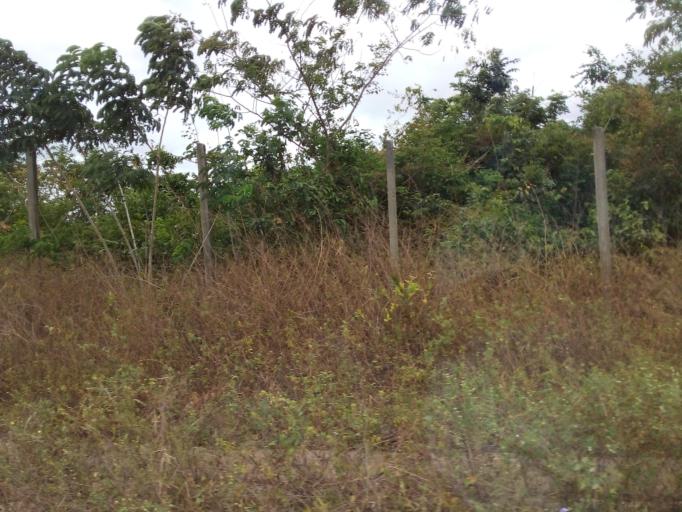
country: BR
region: Maranhao
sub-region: Sao Luis
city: Sao Luis
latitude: -2.6710
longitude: -44.2946
